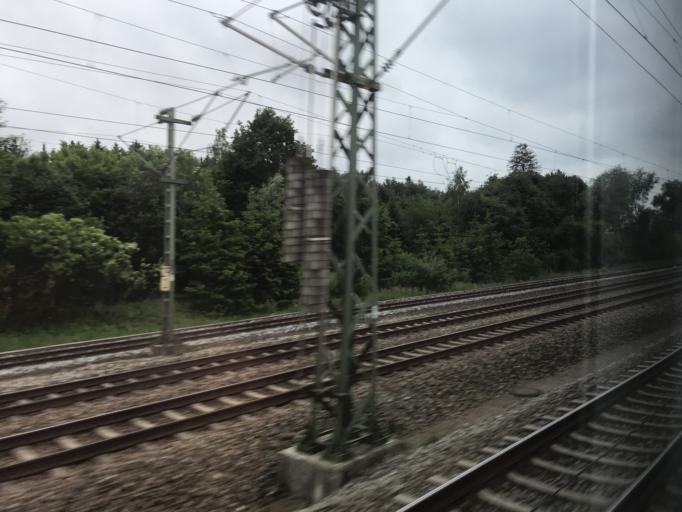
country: DE
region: Bavaria
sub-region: Upper Bavaria
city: Oberschweinbach
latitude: 48.2163
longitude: 11.1995
